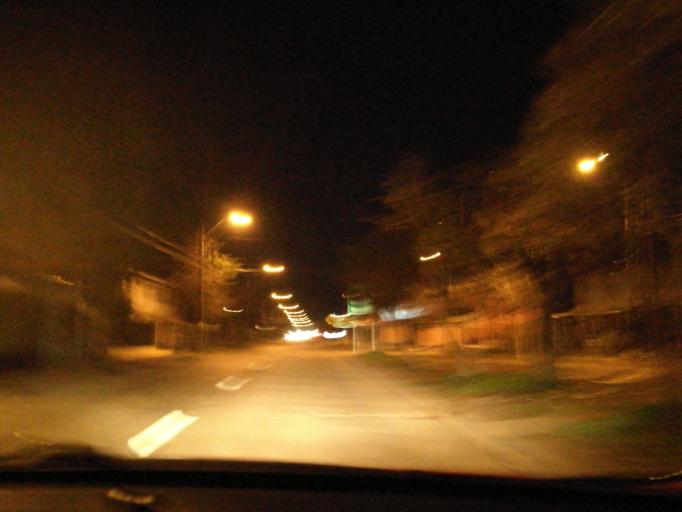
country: CL
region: O'Higgins
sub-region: Provincia de Cachapoal
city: Rancagua
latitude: -34.1819
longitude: -70.7436
